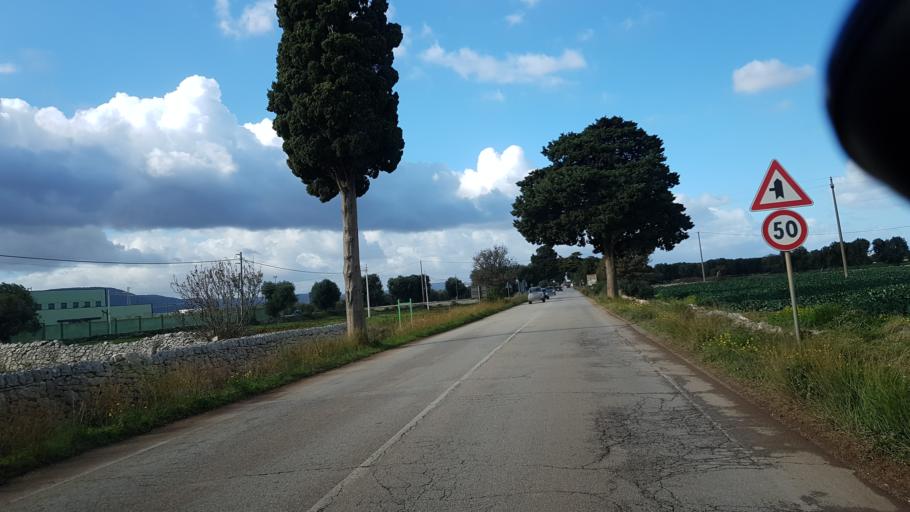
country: IT
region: Apulia
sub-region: Provincia di Brindisi
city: Montalbano
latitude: 40.7871
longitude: 17.4700
